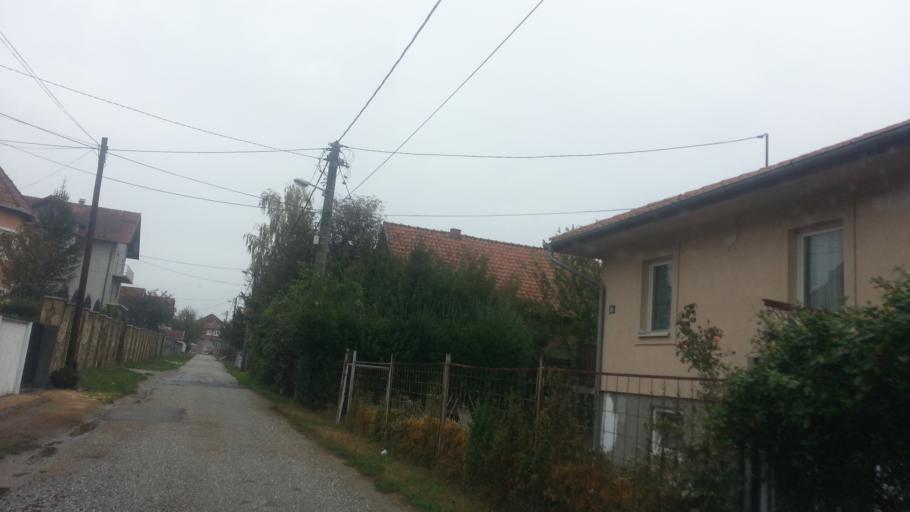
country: RS
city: Novi Banovci
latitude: 44.9058
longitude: 20.2913
